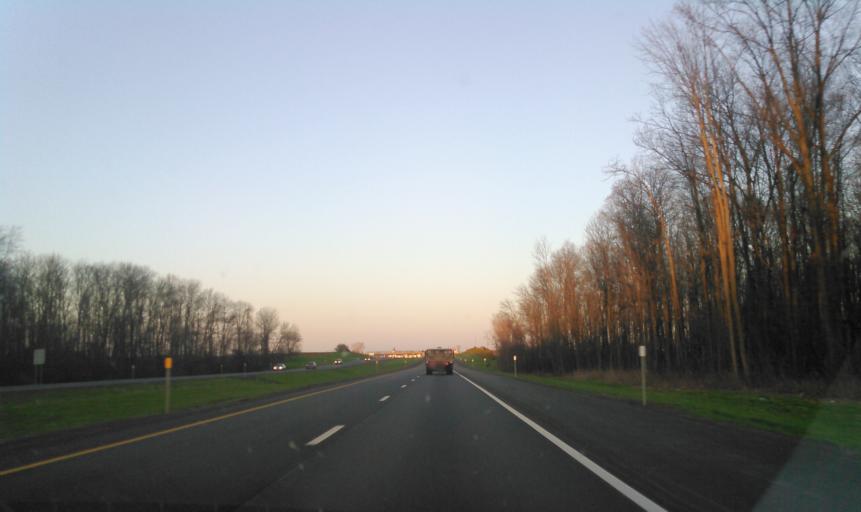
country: US
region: New York
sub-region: Seneca County
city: Waterloo
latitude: 42.9587
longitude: -76.9347
